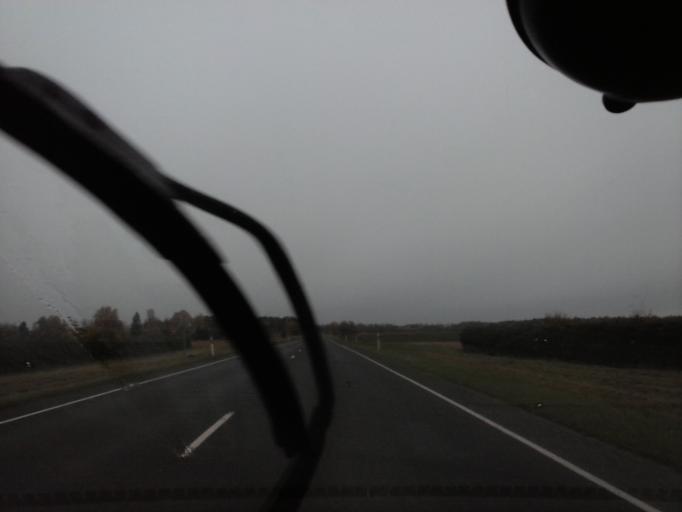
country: EE
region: Viljandimaa
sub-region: Vohma linn
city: Vohma
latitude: 58.7020
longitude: 25.6233
